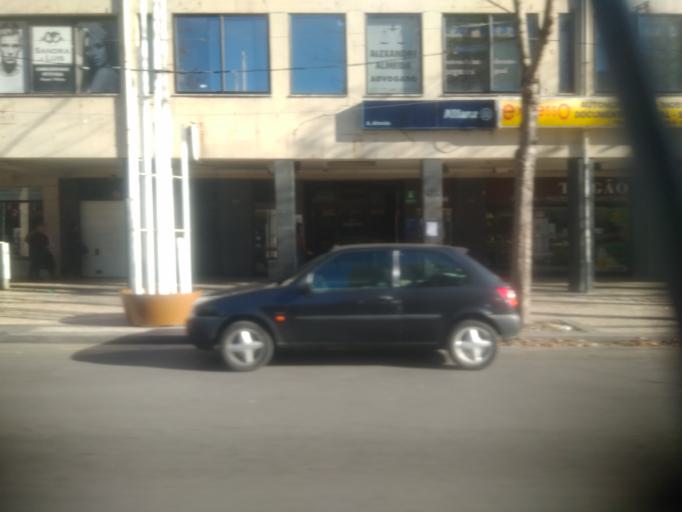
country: PT
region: Porto
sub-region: Vila Nova de Gaia
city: Vila Nova de Gaia
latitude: 41.1270
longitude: -8.6054
